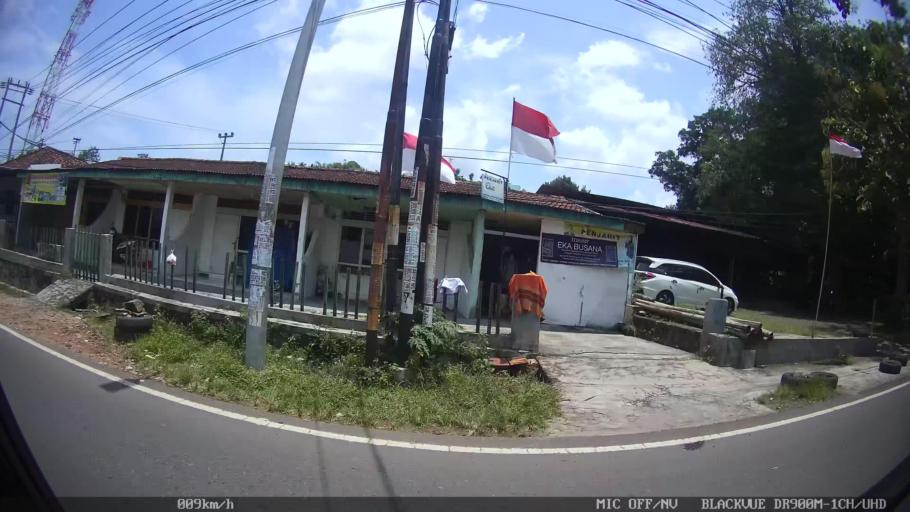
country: ID
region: Lampung
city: Kedaton
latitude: -5.4013
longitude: 105.2550
